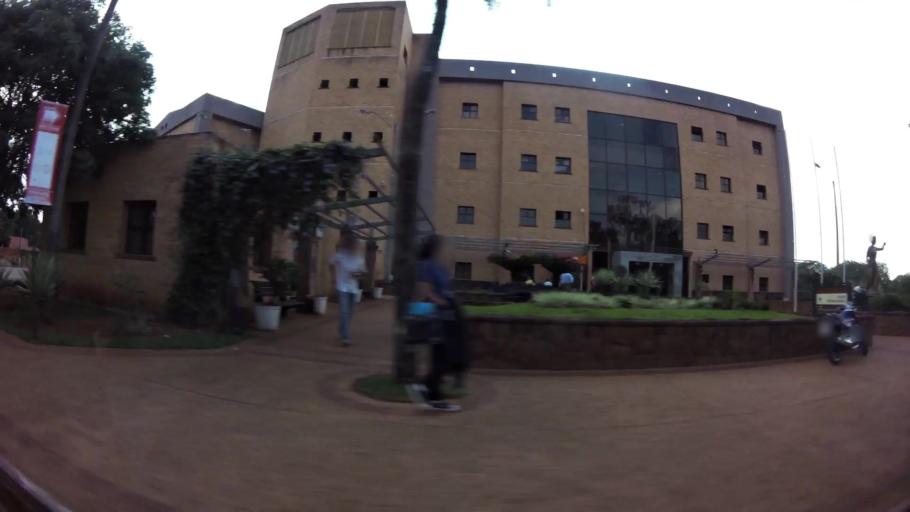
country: PY
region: Central
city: Fernando de la Mora
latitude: -25.3665
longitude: -57.5240
